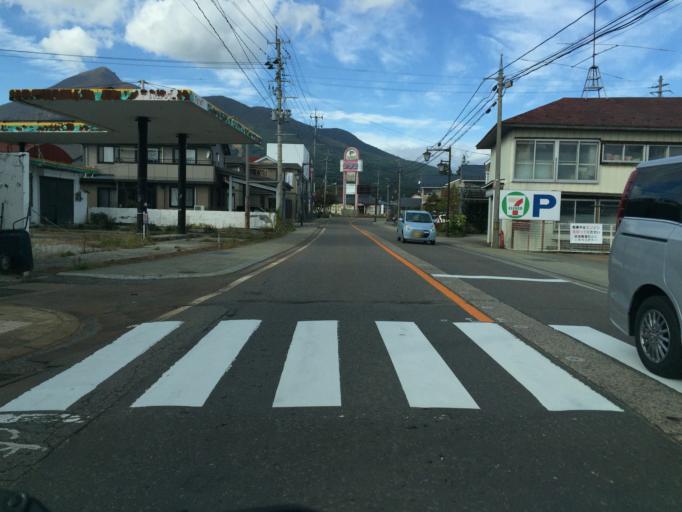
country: JP
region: Fukushima
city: Inawashiro
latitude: 37.5539
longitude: 140.1059
